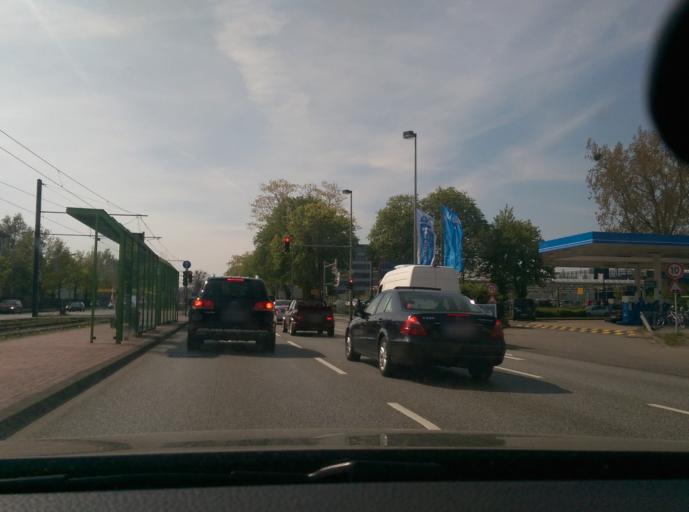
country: DE
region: Lower Saxony
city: Langenhagen
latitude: 52.4241
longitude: 9.7326
